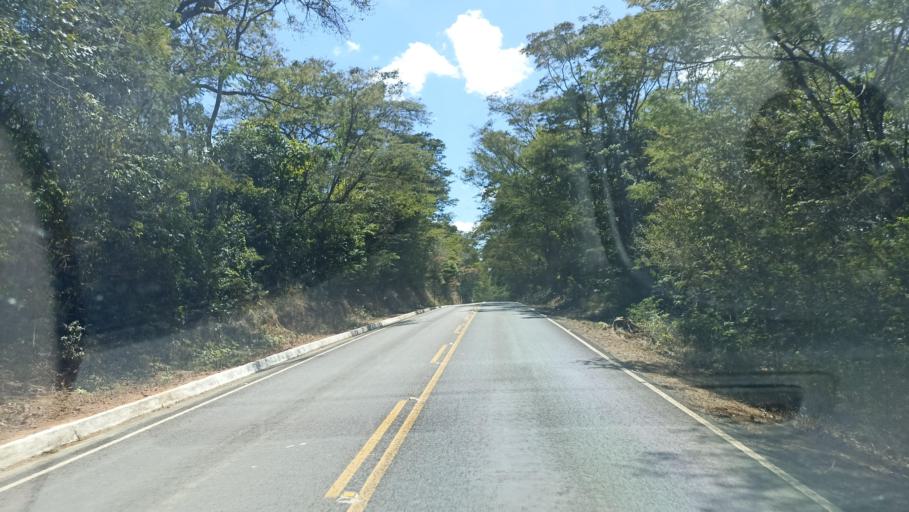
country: BR
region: Bahia
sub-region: Andarai
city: Vera Cruz
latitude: -12.7728
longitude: -41.3304
